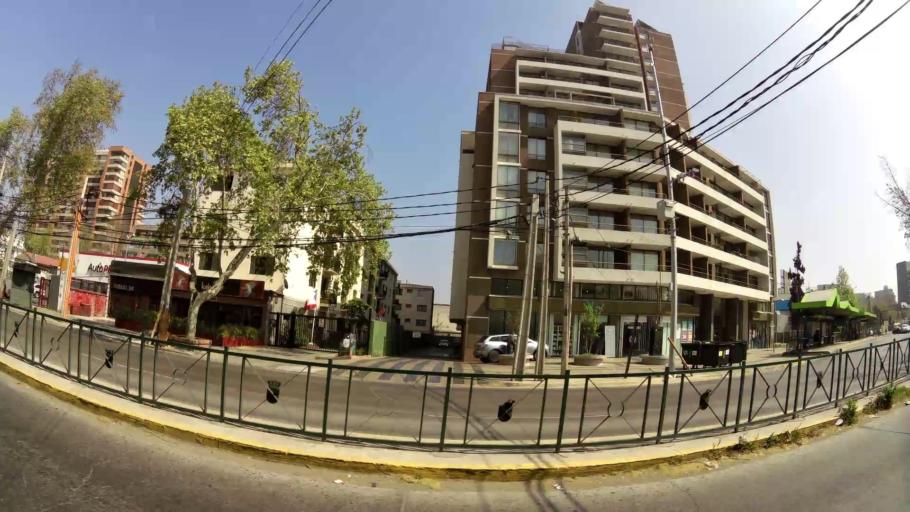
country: CL
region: Santiago Metropolitan
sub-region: Provincia de Santiago
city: Villa Presidente Frei, Nunoa, Santiago, Chile
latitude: -33.4558
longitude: -70.5978
